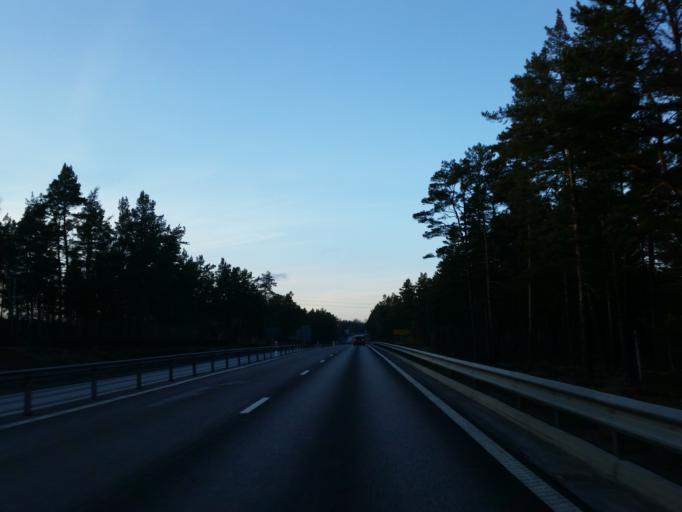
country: SE
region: Kalmar
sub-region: Oskarshamns Kommun
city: Oskarshamn
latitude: 57.3841
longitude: 16.4811
